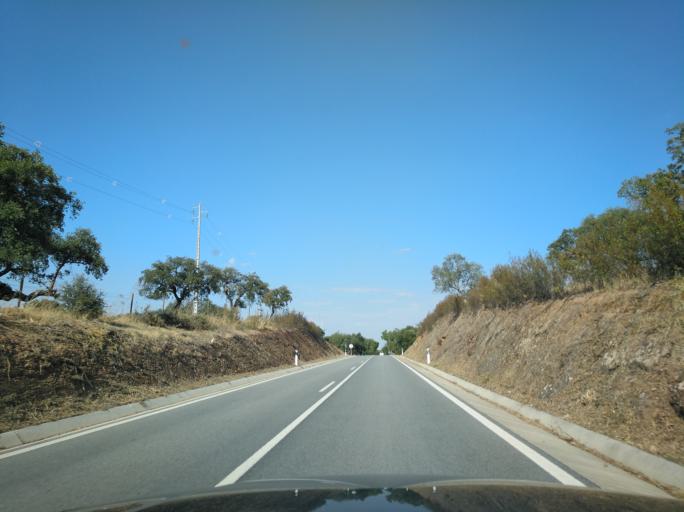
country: ES
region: Andalusia
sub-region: Provincia de Huelva
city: Rosal de la Frontera
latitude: 38.0102
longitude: -7.2748
